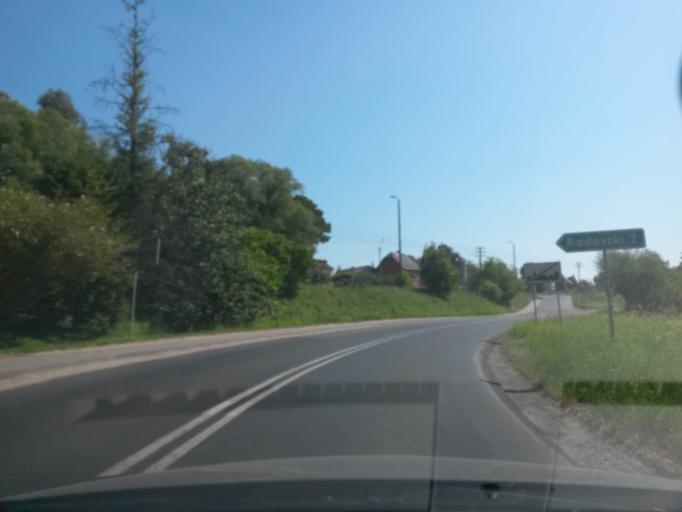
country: PL
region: Kujawsko-Pomorskie
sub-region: Powiat brodnicki
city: Bartniczka
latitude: 53.2498
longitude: 19.6106
